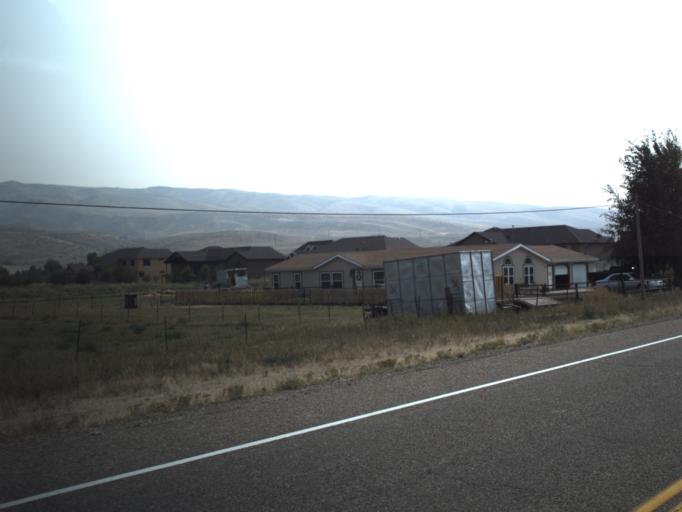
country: US
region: Utah
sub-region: Summit County
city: Coalville
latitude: 41.0258
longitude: -111.5052
